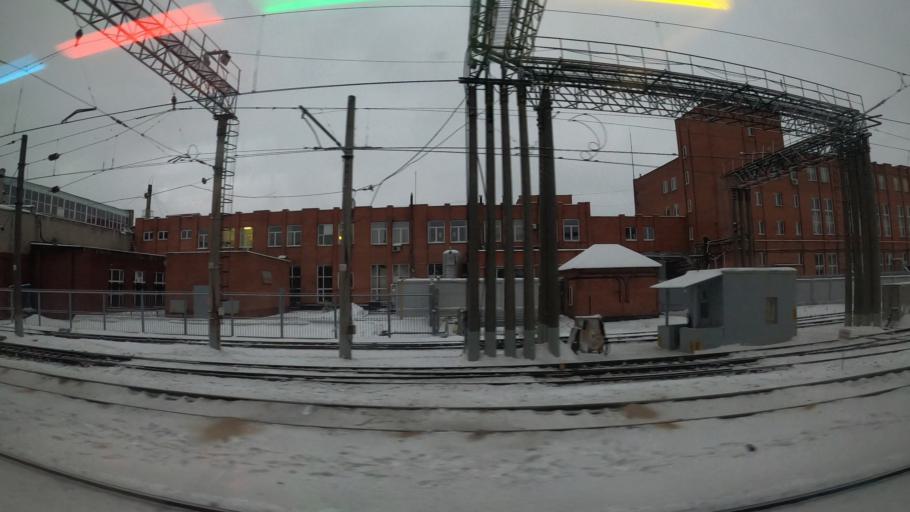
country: RU
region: Vladimir
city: Aleksandrov
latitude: 56.4024
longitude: 38.7104
